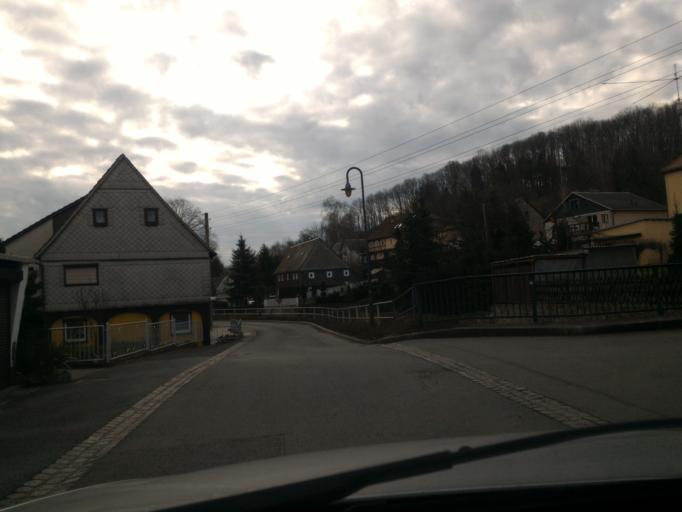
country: DE
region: Saxony
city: Eibau
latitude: 50.9749
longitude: 14.6796
